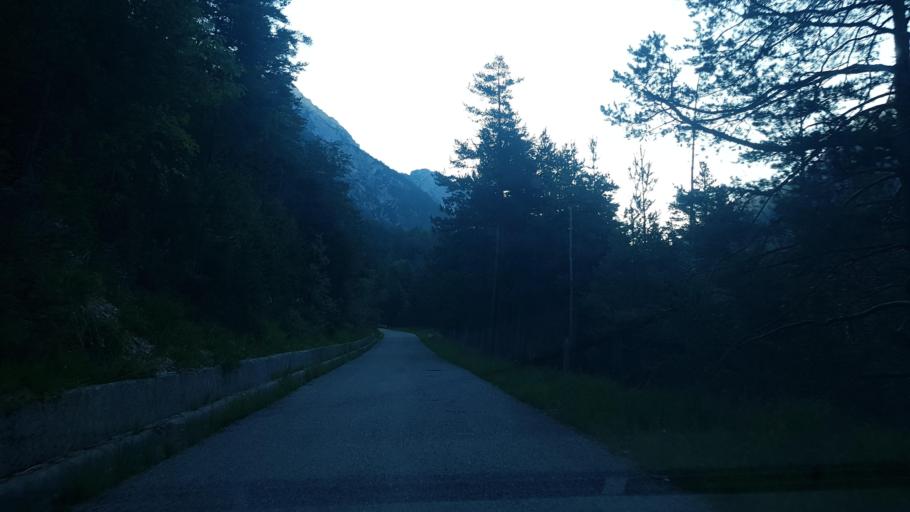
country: IT
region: Friuli Venezia Giulia
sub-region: Provincia di Udine
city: Malborghetto
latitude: 46.4580
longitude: 13.4126
